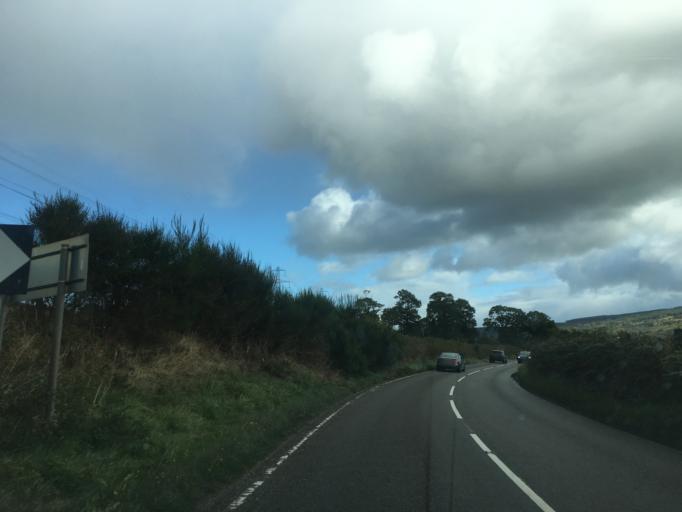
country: GB
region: Scotland
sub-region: Highland
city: Beauly
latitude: 57.4690
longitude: -4.4282
